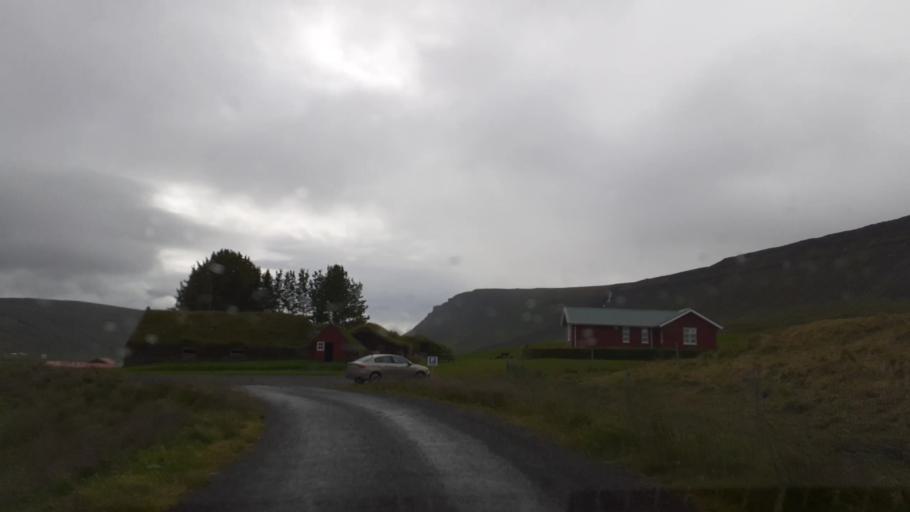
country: IS
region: East
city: Egilsstadir
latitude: 65.6162
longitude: -15.0970
